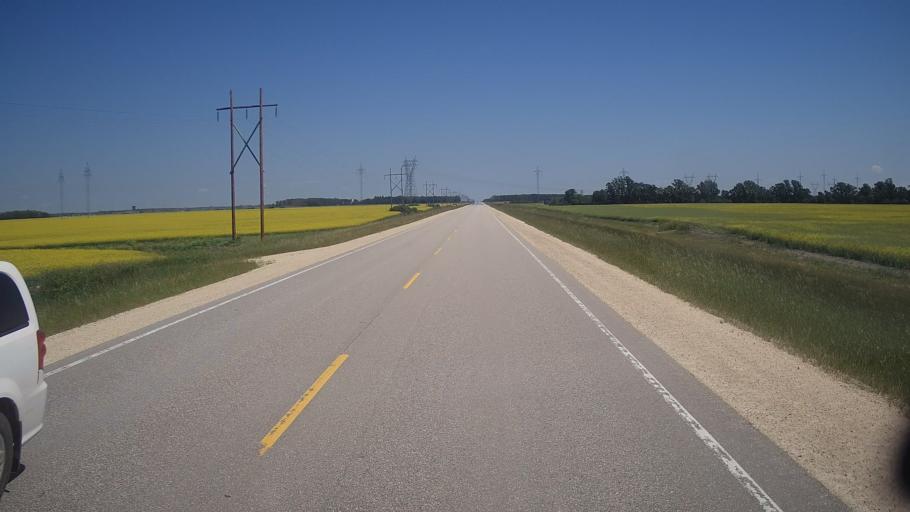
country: CA
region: Manitoba
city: Stonewall
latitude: 50.1227
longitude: -97.4992
